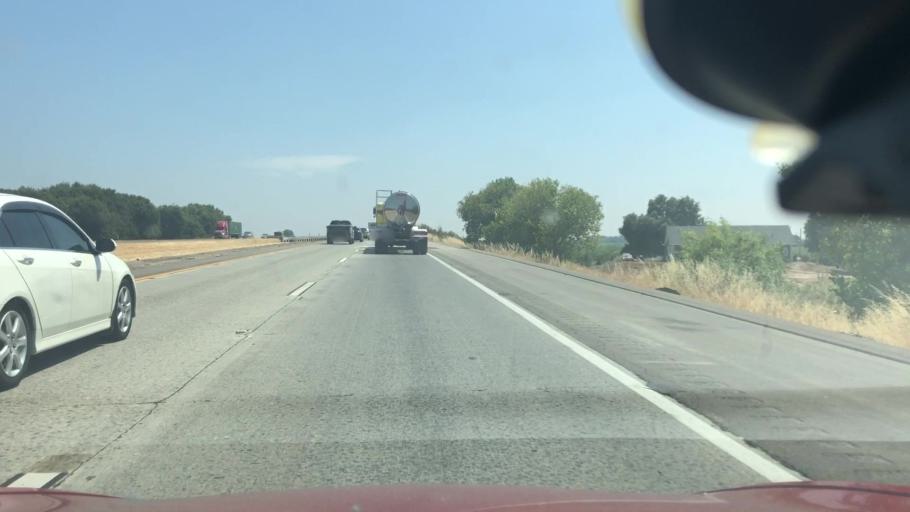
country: US
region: California
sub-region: San Joaquin County
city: Thornton
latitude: 38.2479
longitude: -121.4454
